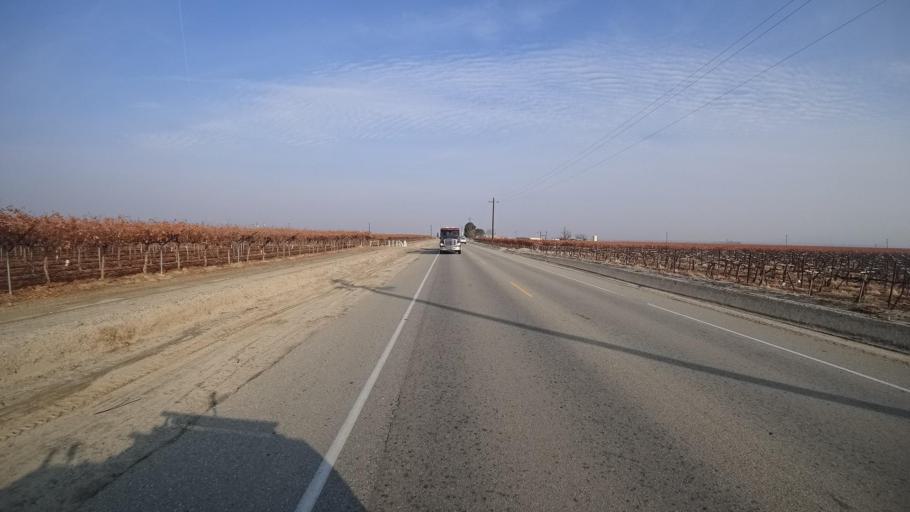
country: US
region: California
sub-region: Kern County
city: Arvin
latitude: 35.0650
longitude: -118.9175
